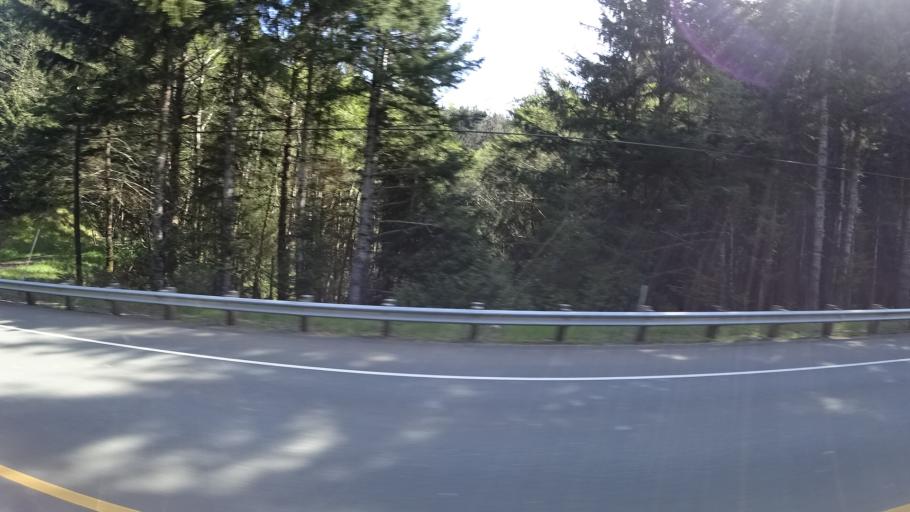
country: US
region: Oregon
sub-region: Curry County
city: Brookings
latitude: 42.1884
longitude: -124.3645
